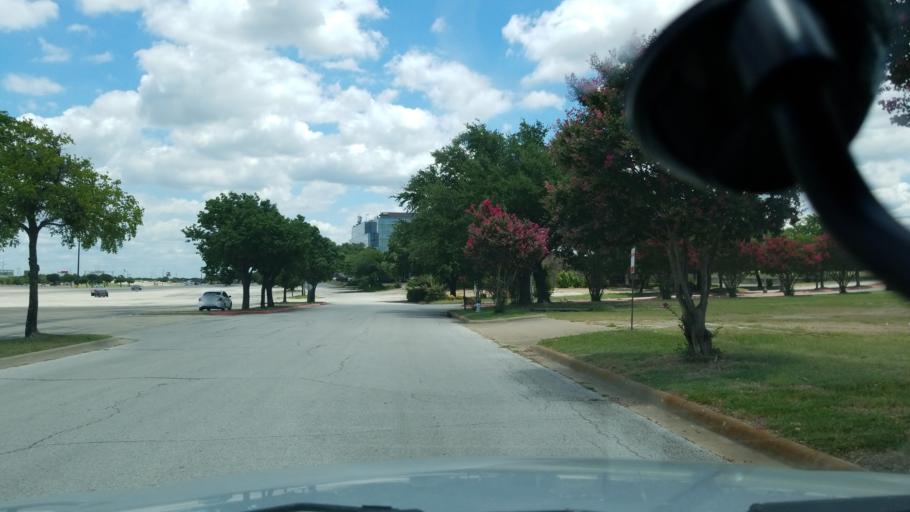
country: US
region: Texas
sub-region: Dallas County
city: Duncanville
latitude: 32.6572
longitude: -96.8779
